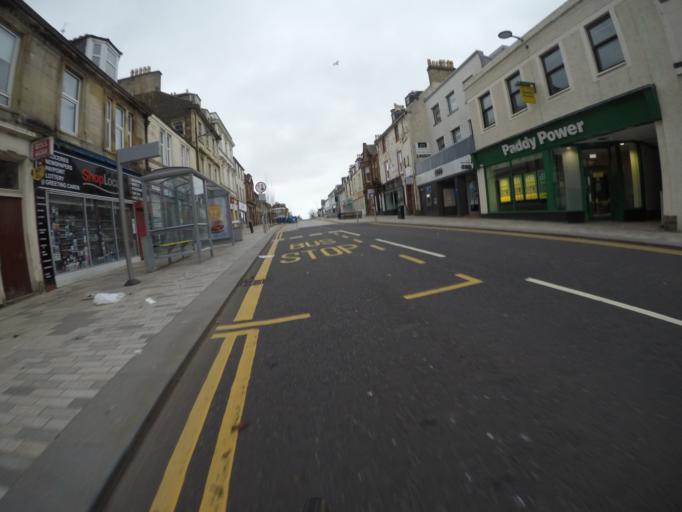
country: GB
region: Scotland
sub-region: North Ayrshire
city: Irvine
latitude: 55.6152
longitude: -4.6677
